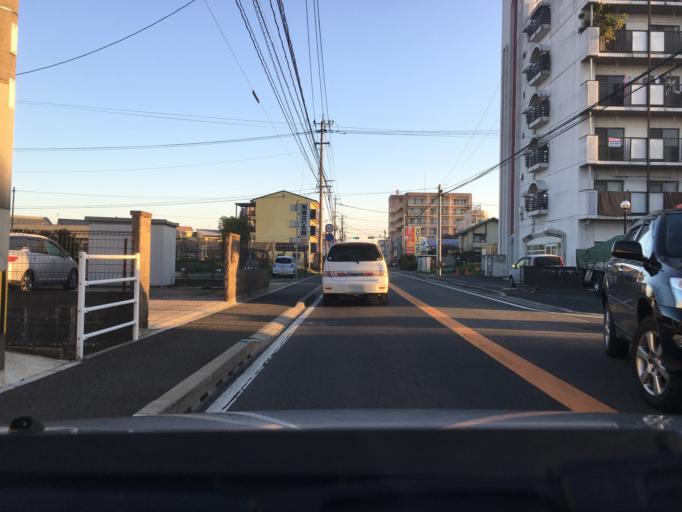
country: JP
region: Fukuoka
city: Kurume
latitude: 33.2949
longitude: 130.4956
